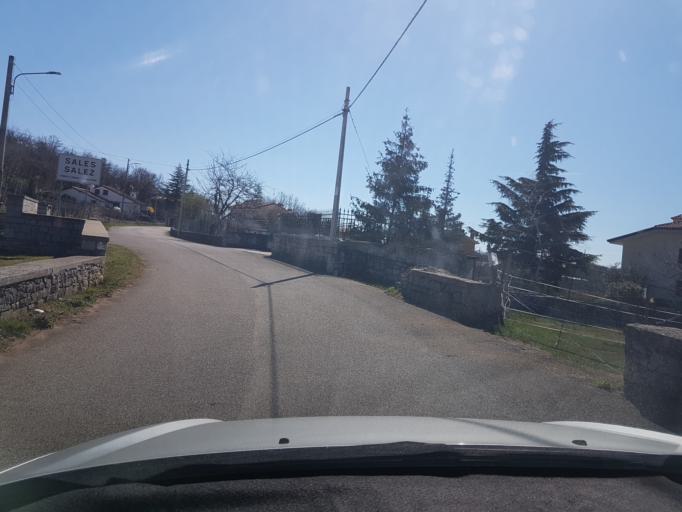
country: IT
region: Friuli Venezia Giulia
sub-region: Provincia di Trieste
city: Sgonico
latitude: 45.7504
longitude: 13.7261
